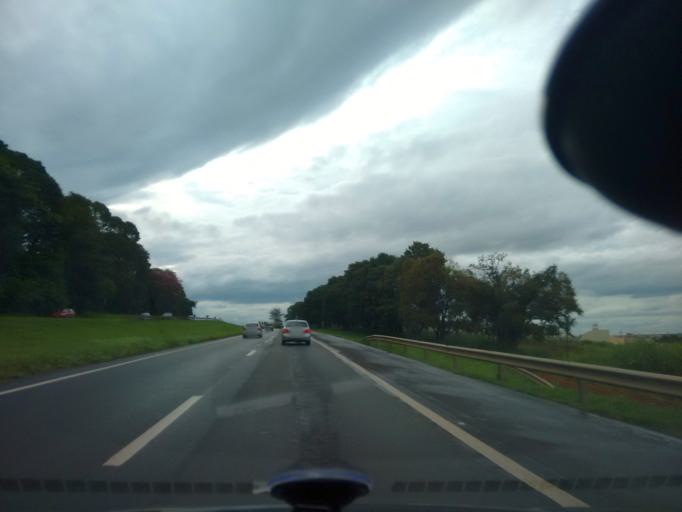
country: BR
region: Sao Paulo
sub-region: Santa Gertrudes
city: Santa Gertrudes
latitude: -22.4635
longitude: -47.5213
